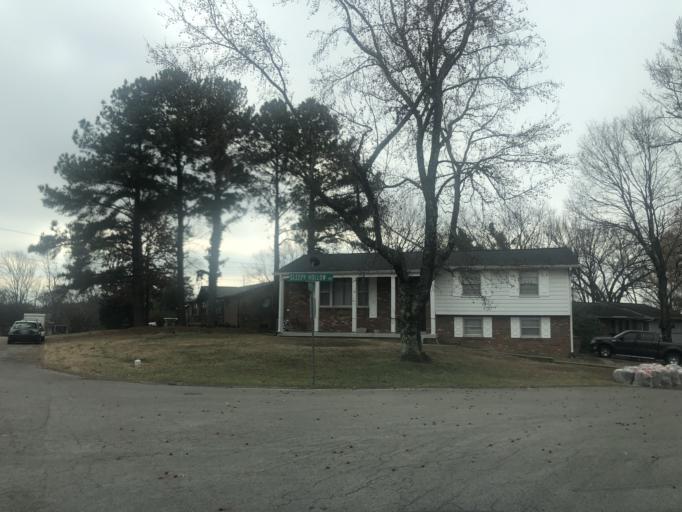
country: US
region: Tennessee
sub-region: Rutherford County
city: La Vergne
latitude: 36.0819
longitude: -86.6414
